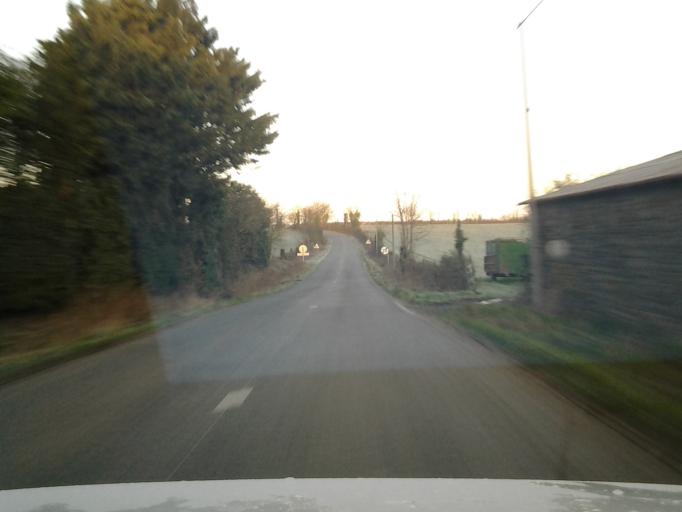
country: FR
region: Pays de la Loire
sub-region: Departement de la Vendee
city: La Verrie
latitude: 46.9265
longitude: -1.0018
